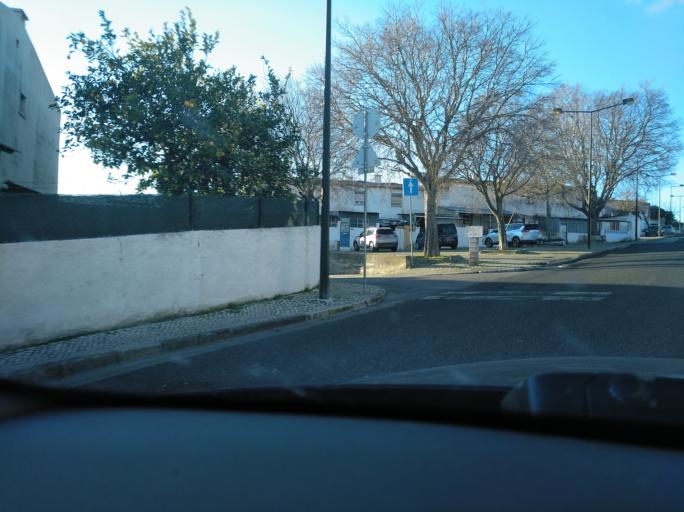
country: PT
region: Lisbon
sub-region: Odivelas
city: Pontinha
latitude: 38.7718
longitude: -9.1868
